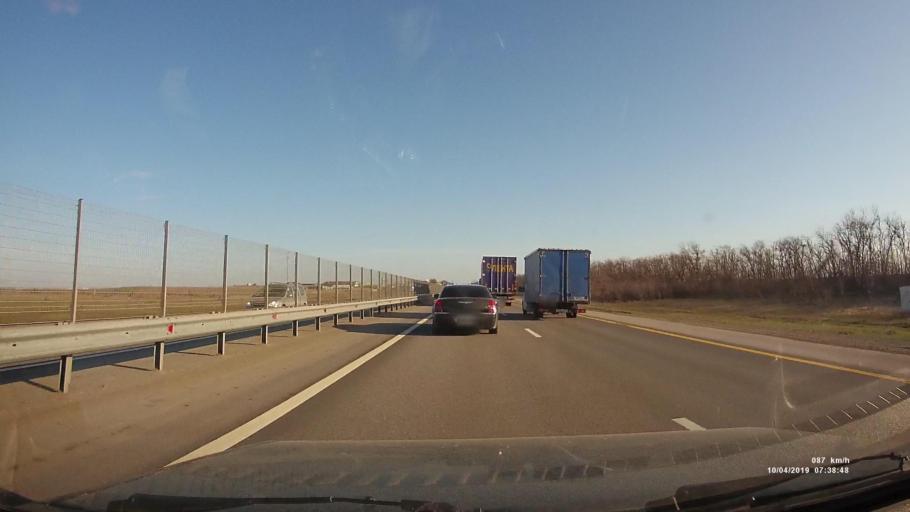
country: RU
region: Rostov
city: Likhoy
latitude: 48.0942
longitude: 40.2596
